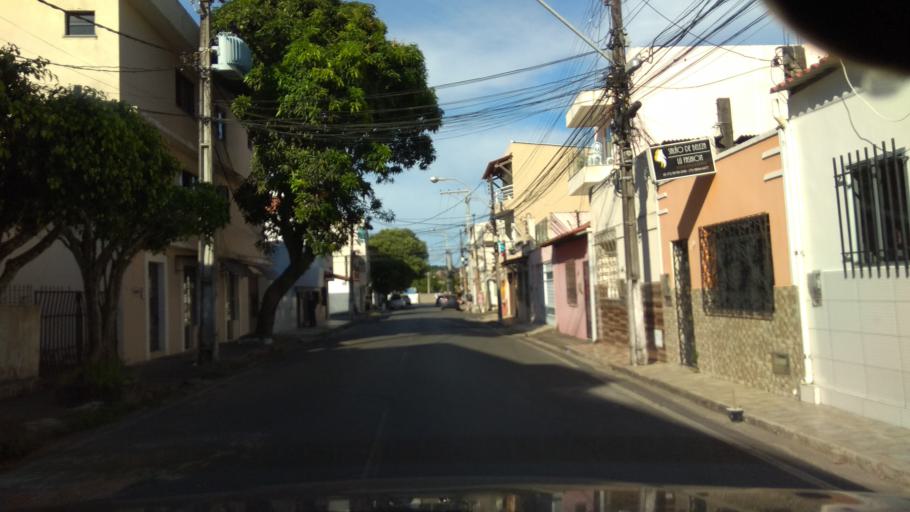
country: BR
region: Bahia
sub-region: Ilheus
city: Ilheus
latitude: -14.8125
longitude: -39.0331
